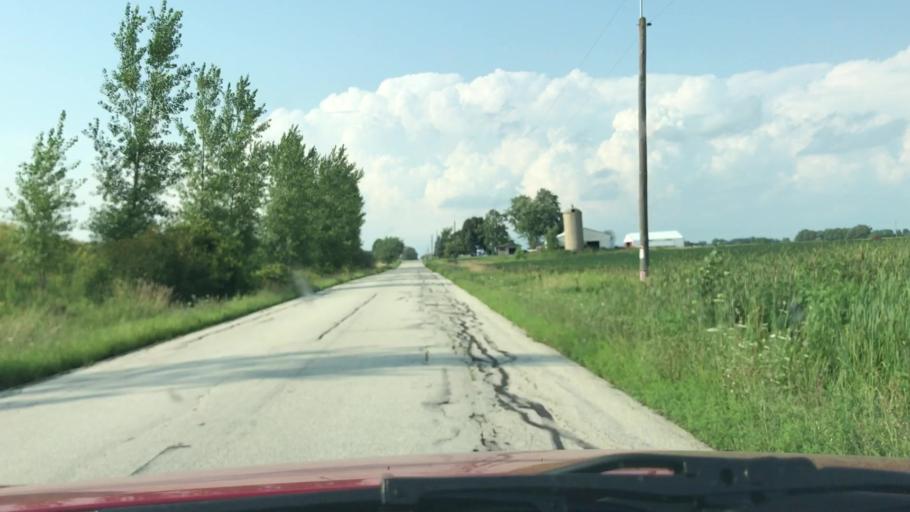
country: US
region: Wisconsin
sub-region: Brown County
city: Oneida
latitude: 44.4411
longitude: -88.1704
